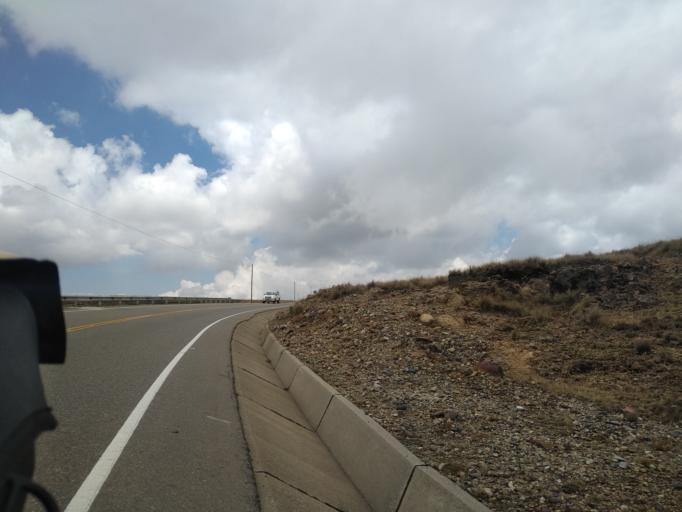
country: PE
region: La Libertad
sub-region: Provincia de Santiago de Chuco
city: Quiruvilca
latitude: -7.9638
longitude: -78.1980
